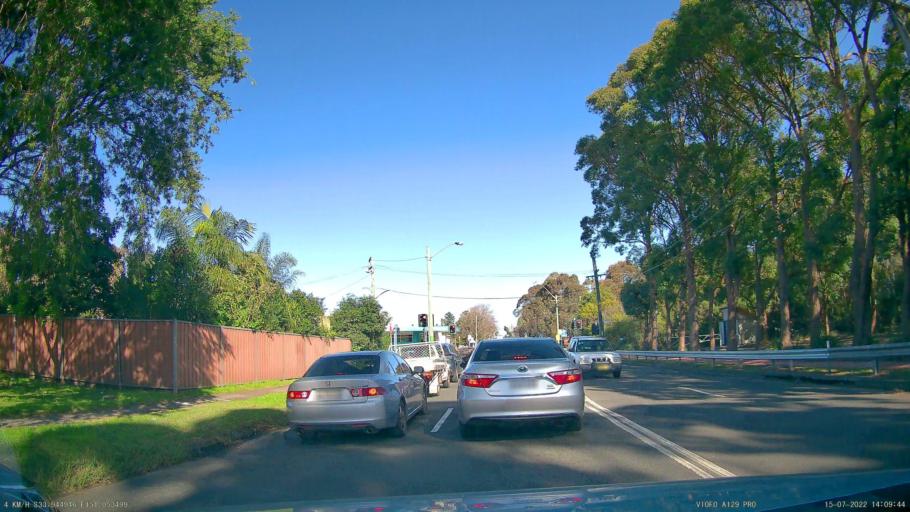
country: AU
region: New South Wales
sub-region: Hurstville
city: Peakhurst
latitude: -33.9449
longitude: 151.0535
